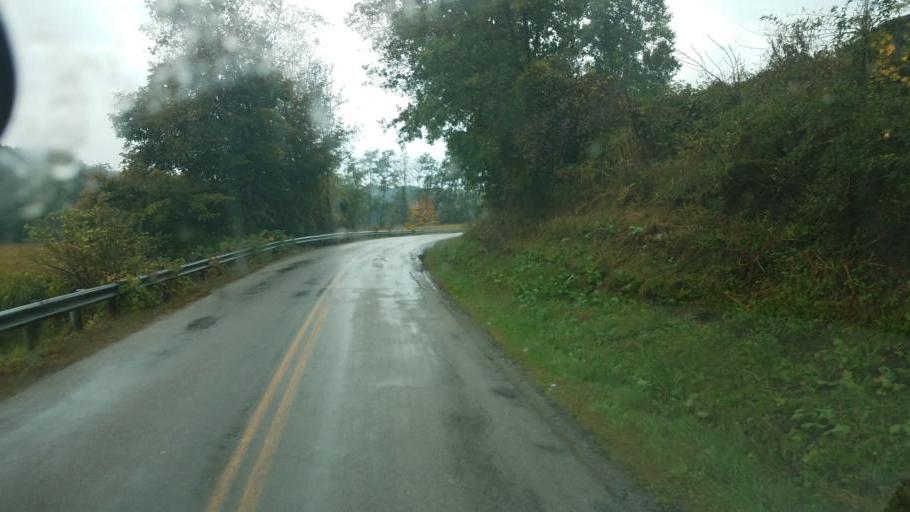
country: US
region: Ohio
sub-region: Sandusky County
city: Bellville
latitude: 40.6236
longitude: -82.3852
